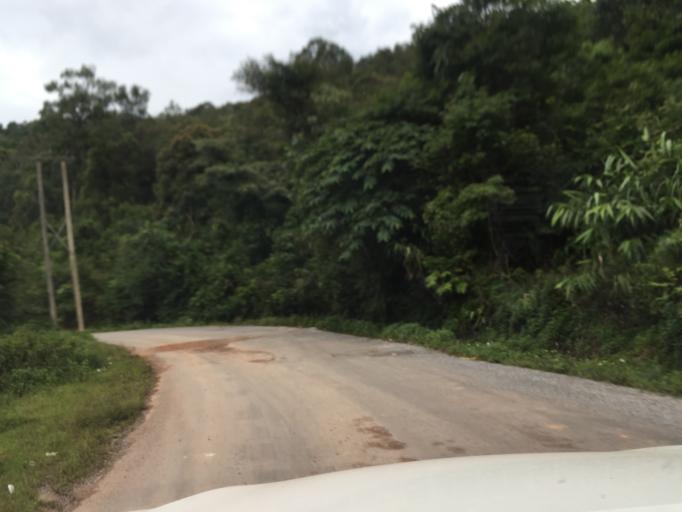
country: LA
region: Phongsali
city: Phongsali
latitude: 21.3282
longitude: 102.0531
